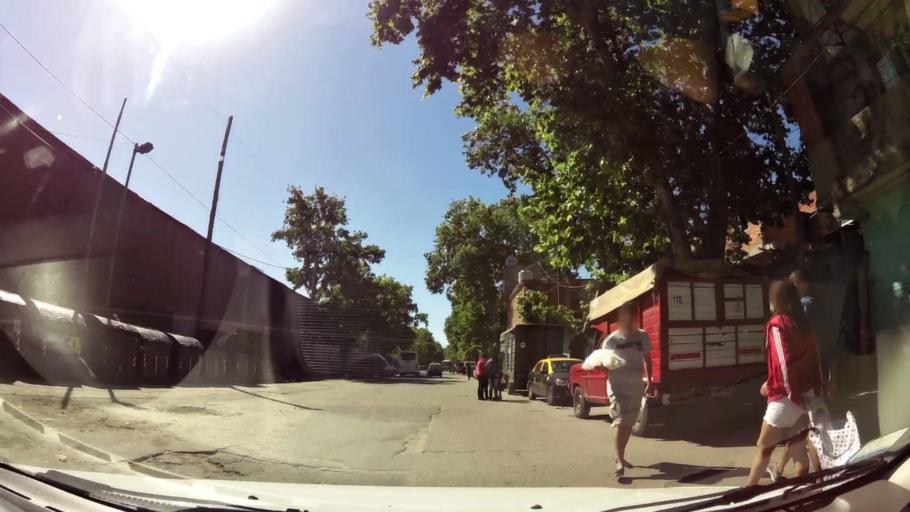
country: AR
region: Buenos Aires F.D.
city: Retiro
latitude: -34.5827
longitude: -58.3783
